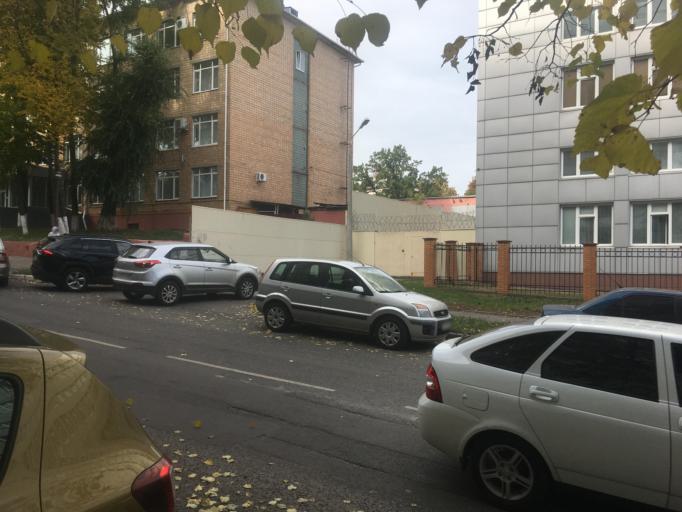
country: RU
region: Kursk
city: Kursk
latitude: 51.7458
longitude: 36.2001
